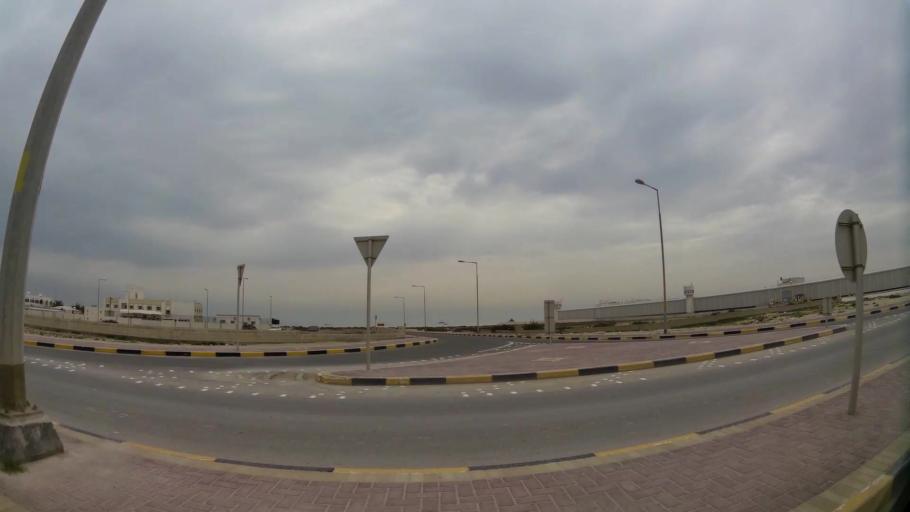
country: BH
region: Central Governorate
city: Dar Kulayb
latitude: 25.9958
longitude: 50.6165
